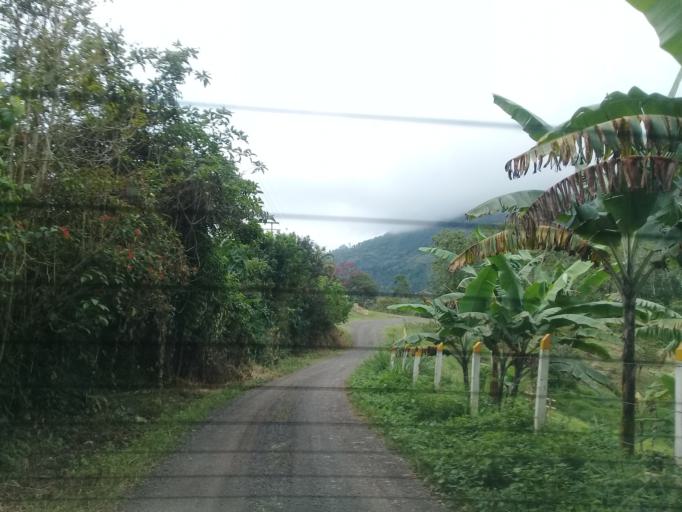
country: CO
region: Cundinamarca
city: Viani
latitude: 4.8407
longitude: -74.5451
